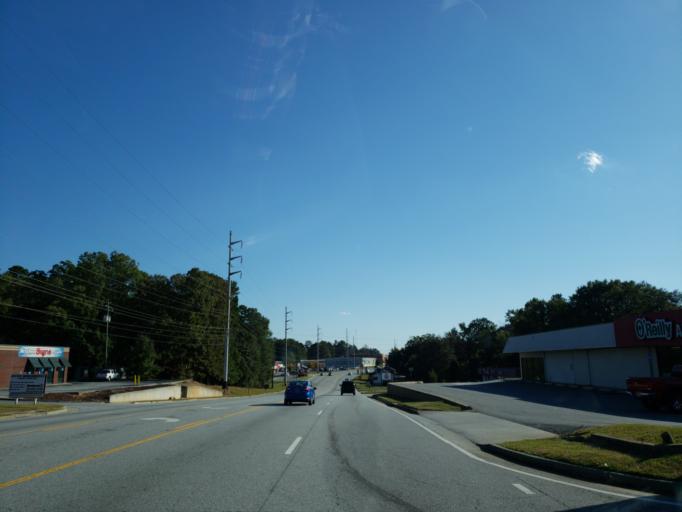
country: US
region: Georgia
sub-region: Gwinnett County
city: Lawrenceville
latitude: 33.9716
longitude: -83.9864
